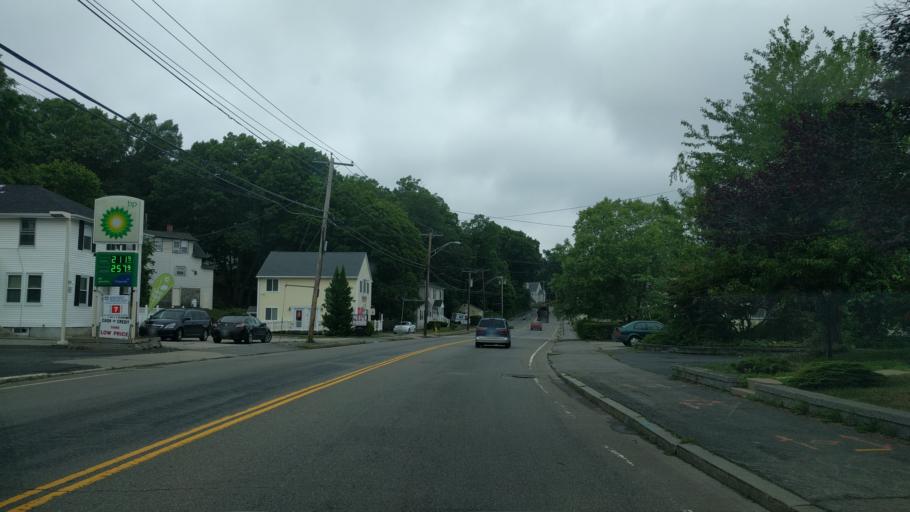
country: US
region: Massachusetts
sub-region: Worcester County
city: Sunderland
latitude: 42.2370
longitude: -71.7521
